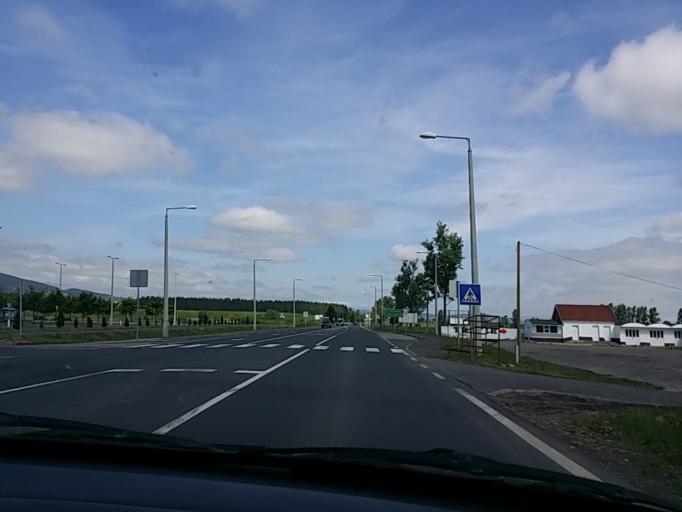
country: HU
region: Borsod-Abauj-Zemplen
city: Satoraljaujhely
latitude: 48.4152
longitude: 21.6460
